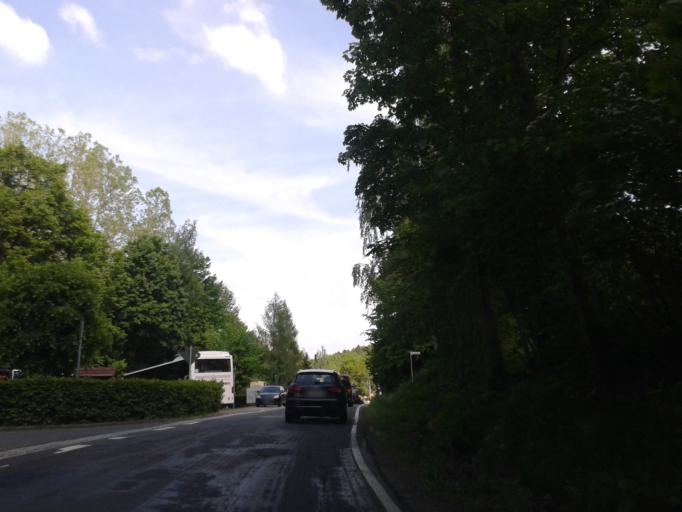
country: DE
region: Saxony
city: Reinsberg
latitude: 51.0100
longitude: 13.3560
